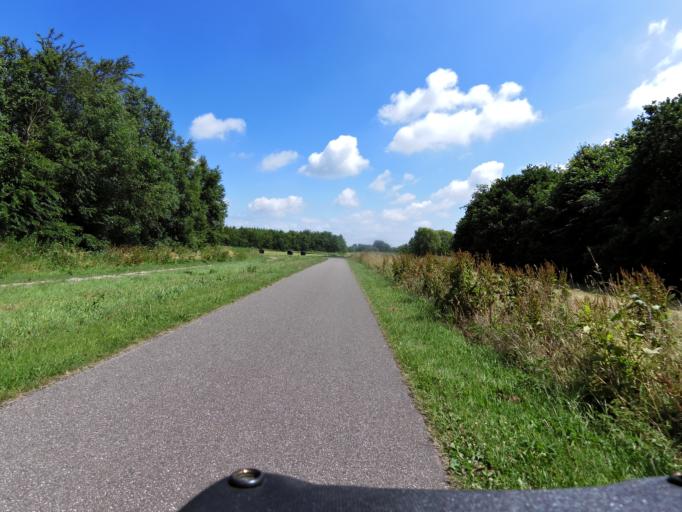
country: NL
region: South Holland
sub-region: Gemeente Delft
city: Delft
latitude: 51.9719
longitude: 4.3701
